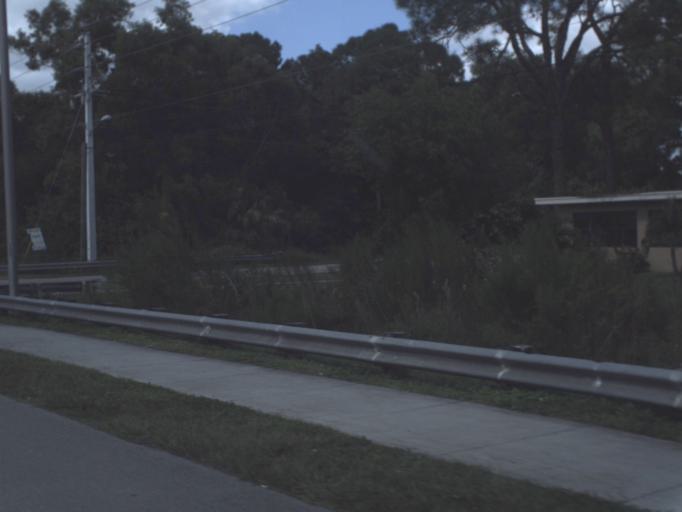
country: US
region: Florida
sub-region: Collier County
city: Naples Manor
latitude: 26.0910
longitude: -81.7331
